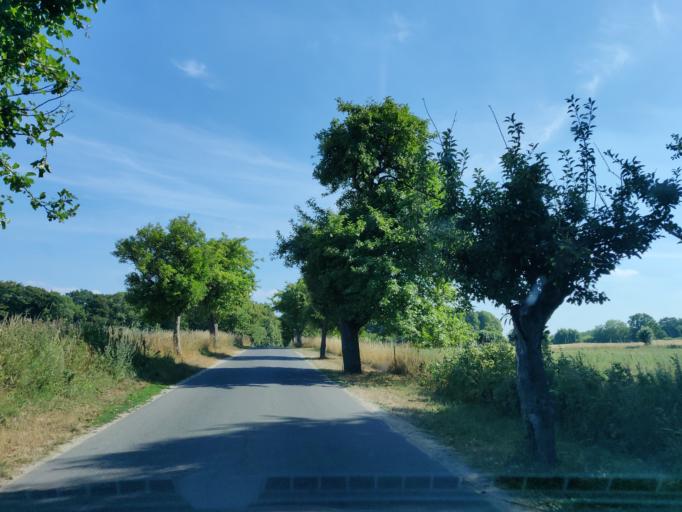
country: DK
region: Zealand
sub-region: Lejre Kommune
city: Lejre
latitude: 55.6080
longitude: 11.9426
